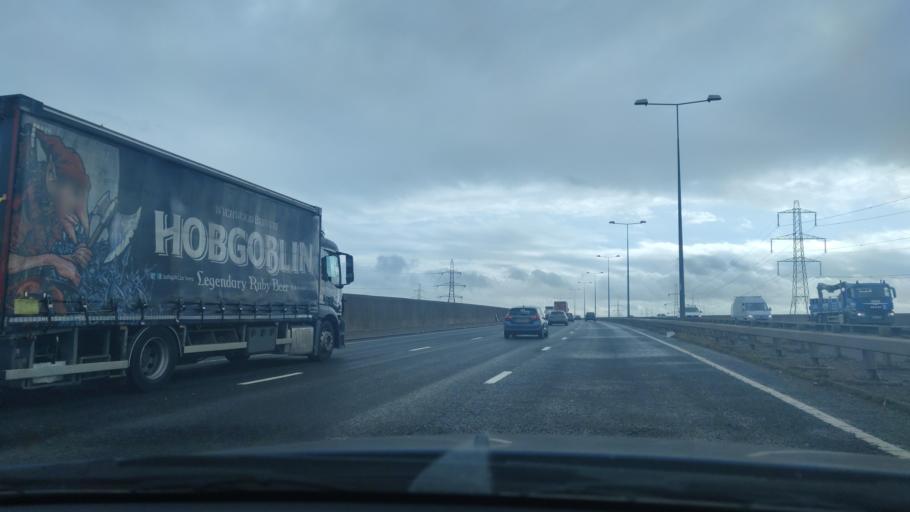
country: GB
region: England
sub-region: Essex
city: Purfleet
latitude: 51.5030
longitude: 0.2114
